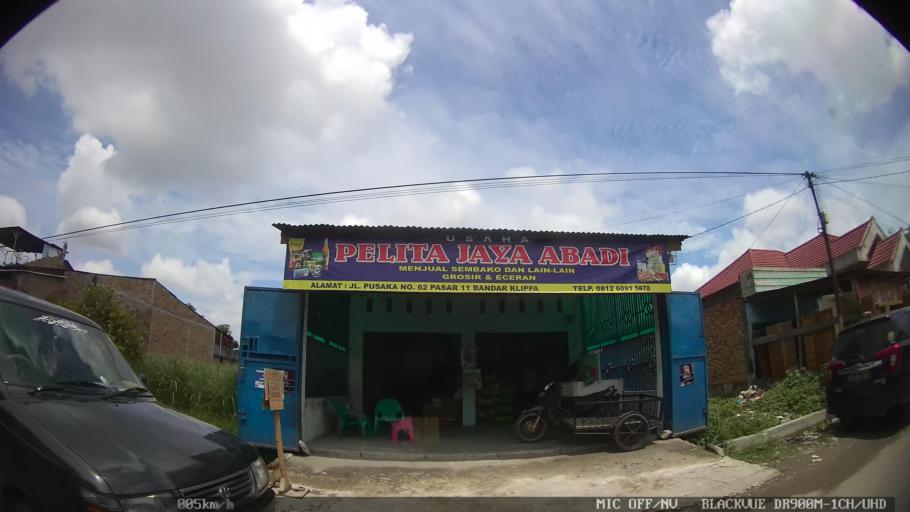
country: ID
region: North Sumatra
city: Medan
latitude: 3.6127
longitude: 98.7614
